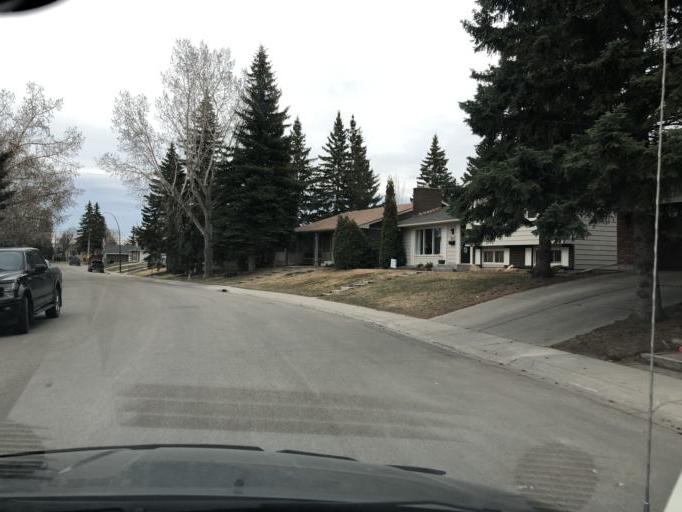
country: CA
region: Alberta
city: Calgary
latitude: 50.9318
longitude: -114.0417
